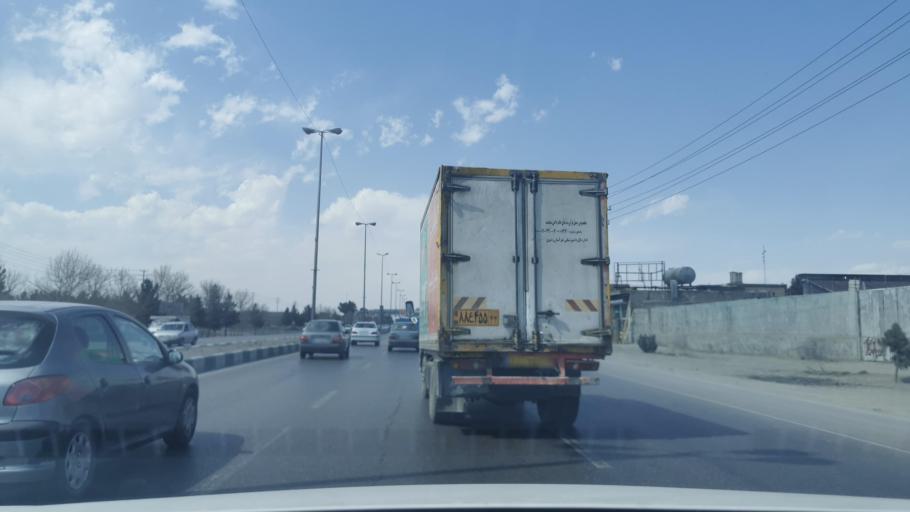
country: IR
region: Razavi Khorasan
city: Mashhad
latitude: 36.4105
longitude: 59.4730
